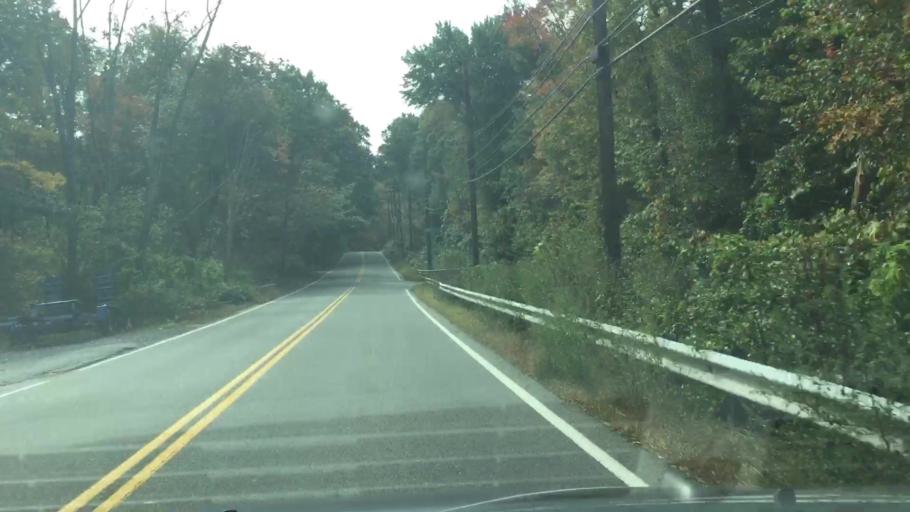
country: US
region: Massachusetts
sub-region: Middlesex County
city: Tewksbury
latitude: 42.6680
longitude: -71.2332
